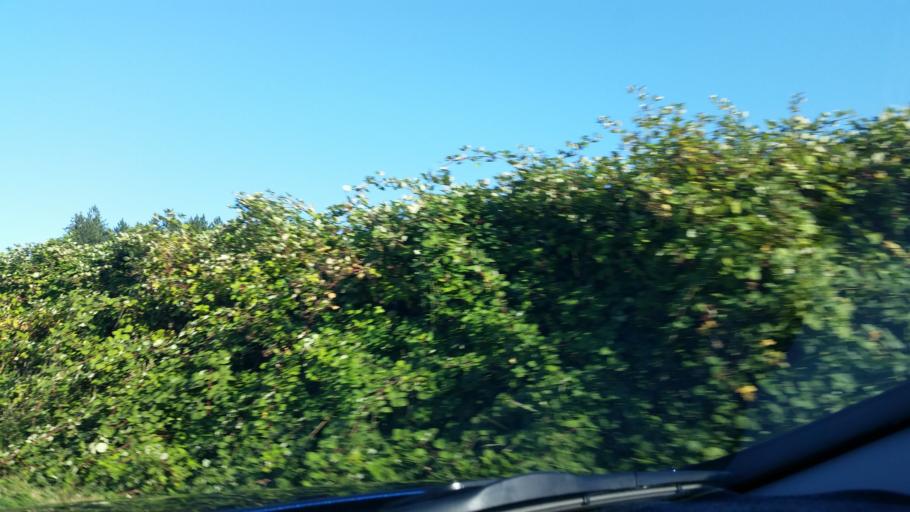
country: US
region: Oregon
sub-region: Marion County
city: Hubbard
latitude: 45.2454
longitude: -122.8837
